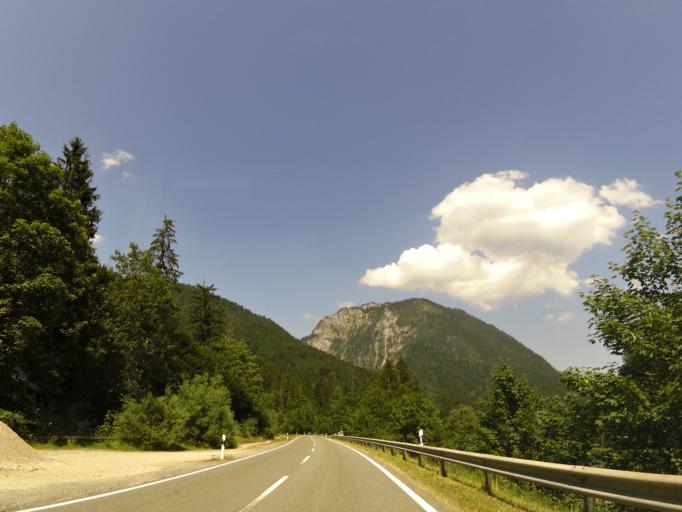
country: DE
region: Bavaria
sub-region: Upper Bavaria
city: Reit im Winkl
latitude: 47.6814
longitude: 12.5493
